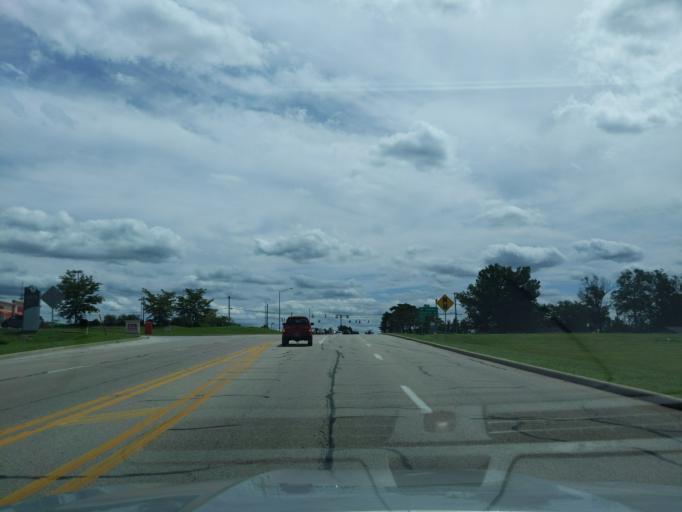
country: US
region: Indiana
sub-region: Ripley County
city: Batesville
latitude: 39.3071
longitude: -85.2197
